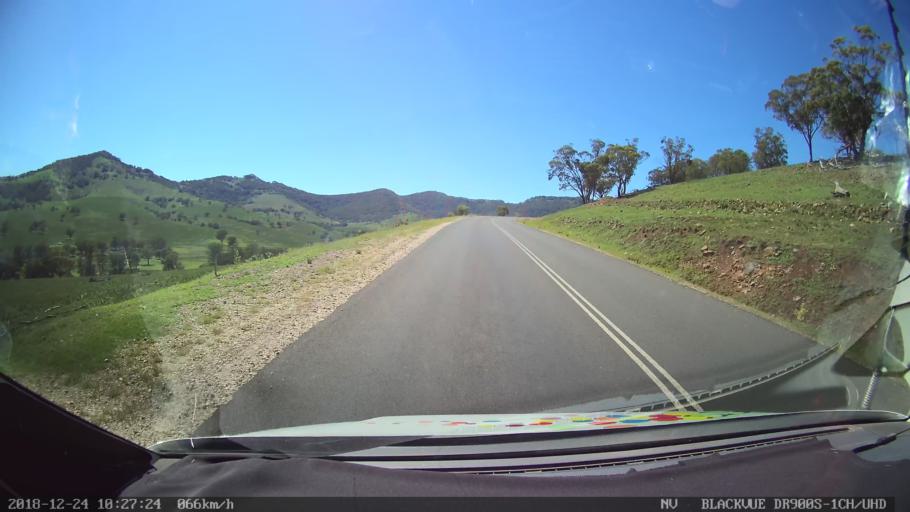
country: AU
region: New South Wales
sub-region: Liverpool Plains
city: Quirindi
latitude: -31.8173
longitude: 150.5325
